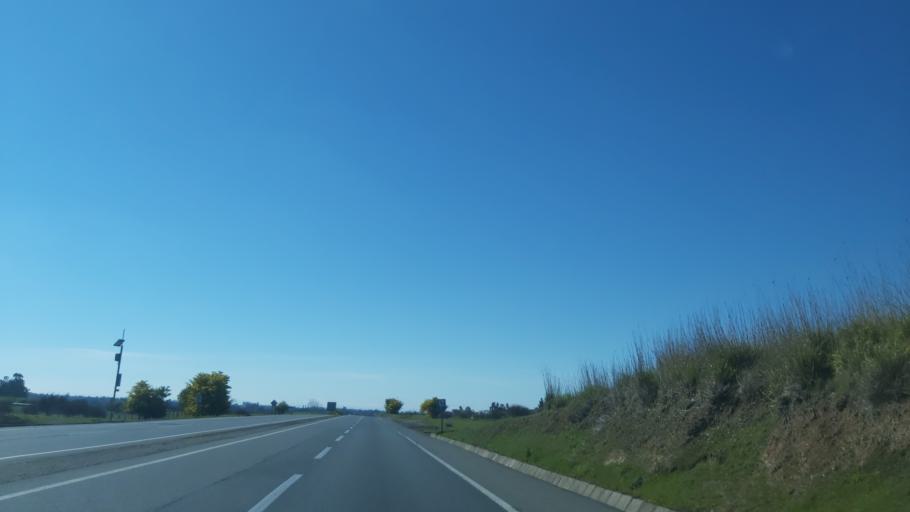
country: CL
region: Biobio
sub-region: Provincia de Nuble
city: Bulnes
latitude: -36.6602
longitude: -72.2561
